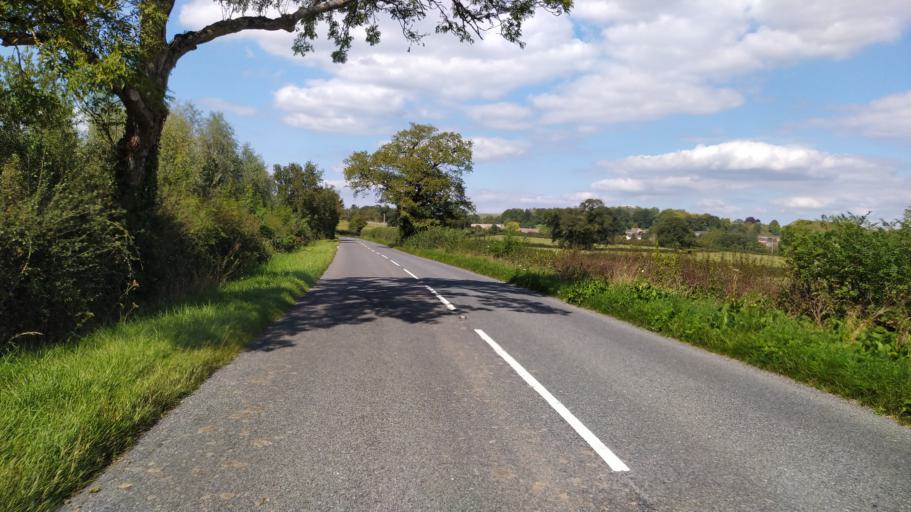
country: GB
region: England
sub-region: Wiltshire
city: Mere
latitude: 51.0814
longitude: -2.2809
